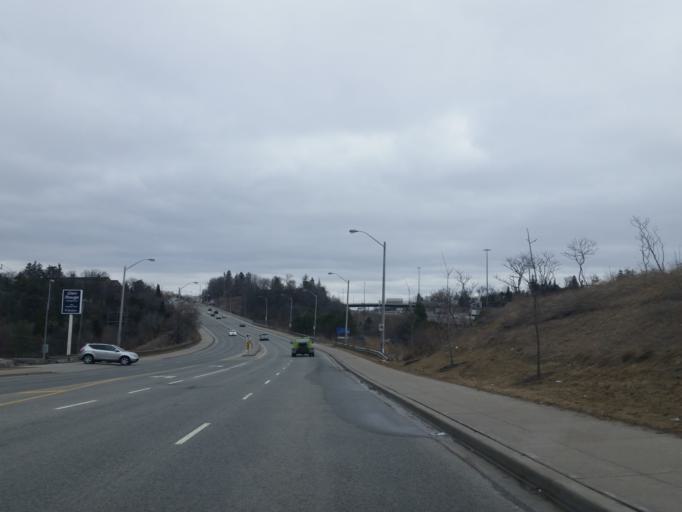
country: CA
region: Ontario
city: Pickering
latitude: 43.8039
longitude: -79.1377
